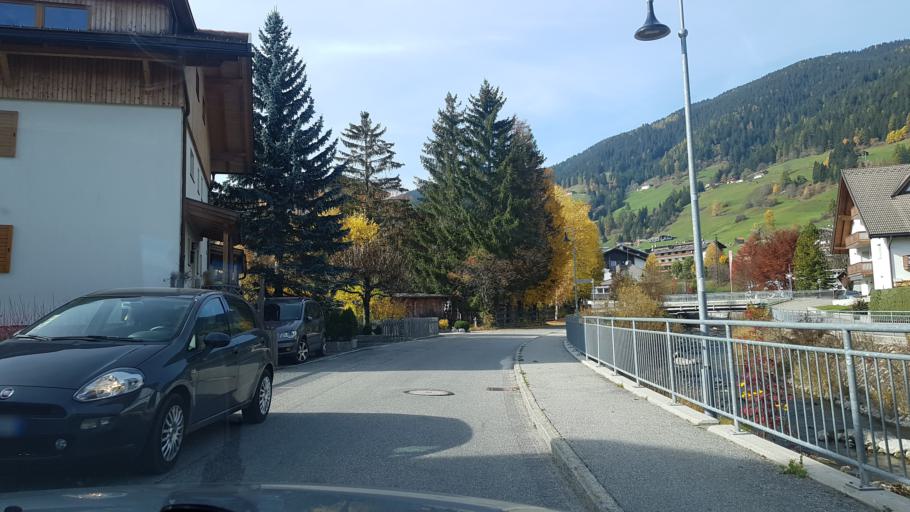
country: IT
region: Trentino-Alto Adige
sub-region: Bolzano
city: San Candido
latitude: 46.7342
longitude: 12.2869
